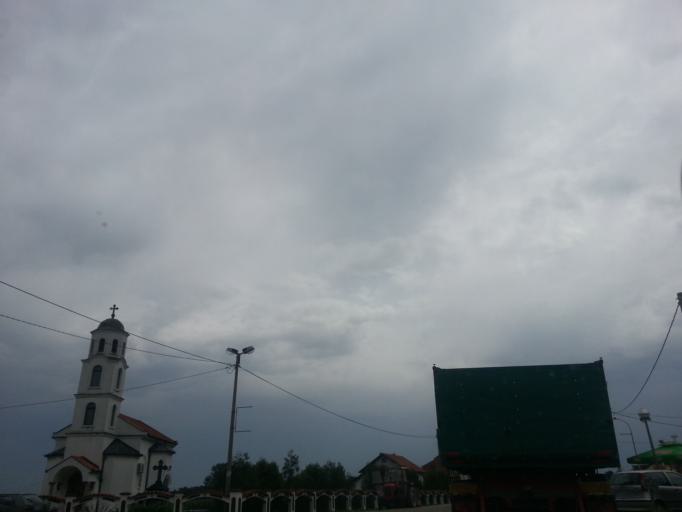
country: BA
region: Republika Srpska
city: Velika Obarska
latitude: 44.8100
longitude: 19.0667
